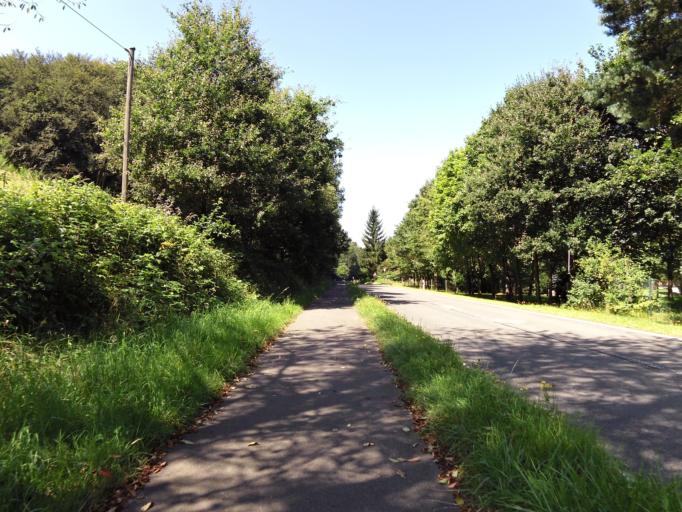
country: DE
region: Rheinland-Pfalz
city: Enkenbach-Alsenborn
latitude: 49.5012
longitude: 7.9012
